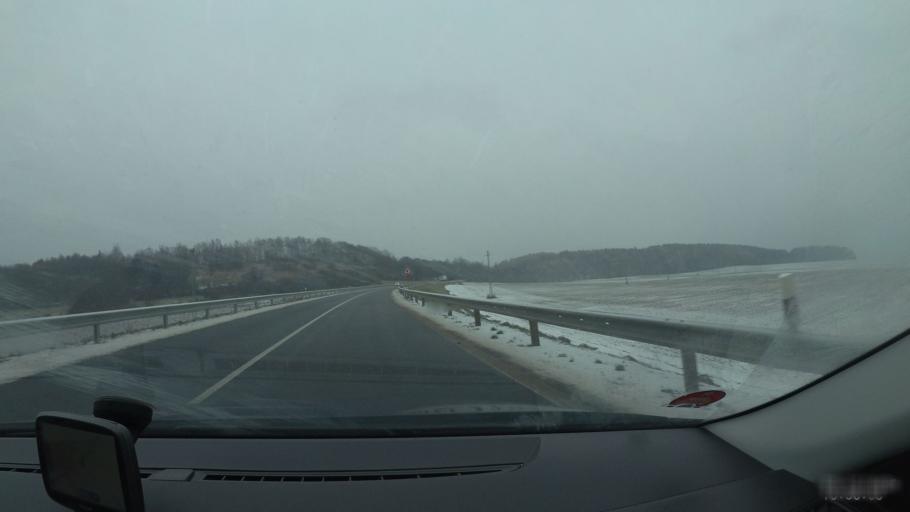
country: CZ
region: Central Bohemia
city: Revnicov
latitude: 50.1880
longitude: 13.8189
